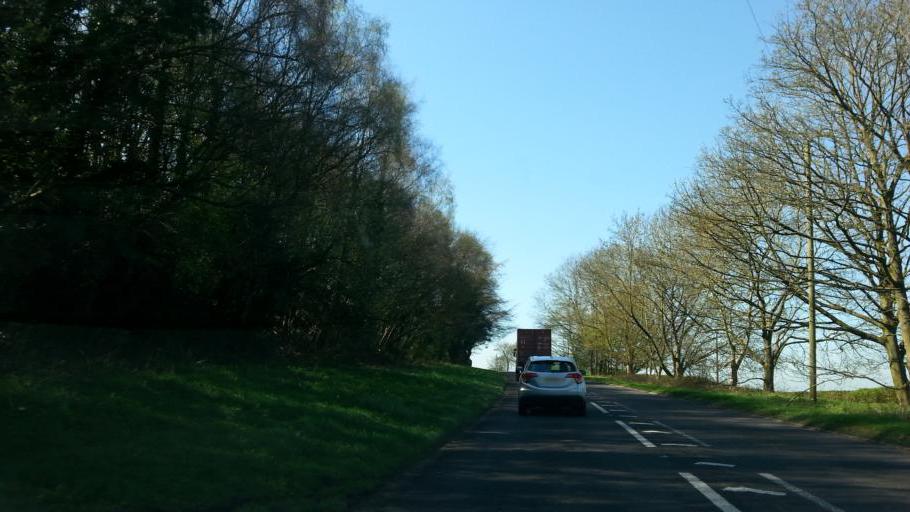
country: GB
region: England
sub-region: Staffordshire
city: Colwich
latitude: 52.8569
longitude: -1.9728
